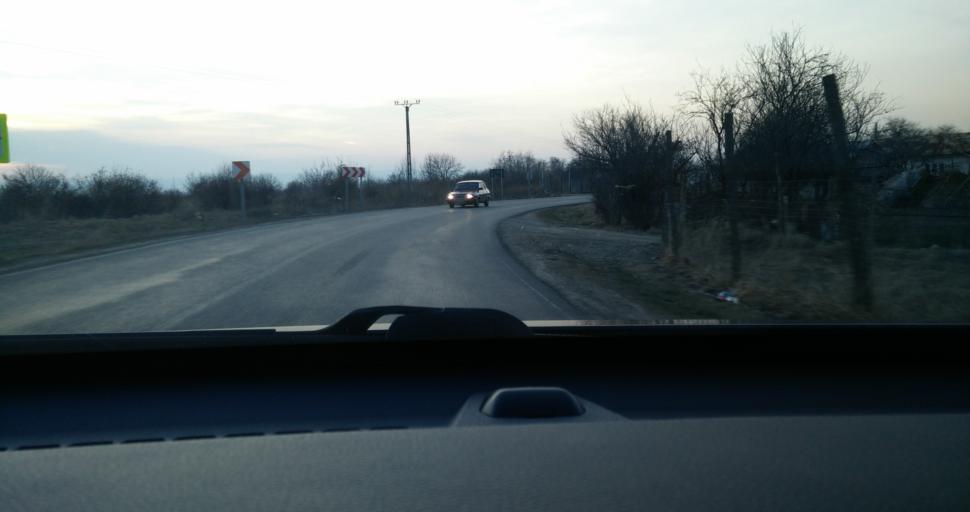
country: RO
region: Vrancea
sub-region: Comuna Milcovul
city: Milcovul
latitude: 45.6778
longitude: 27.2373
